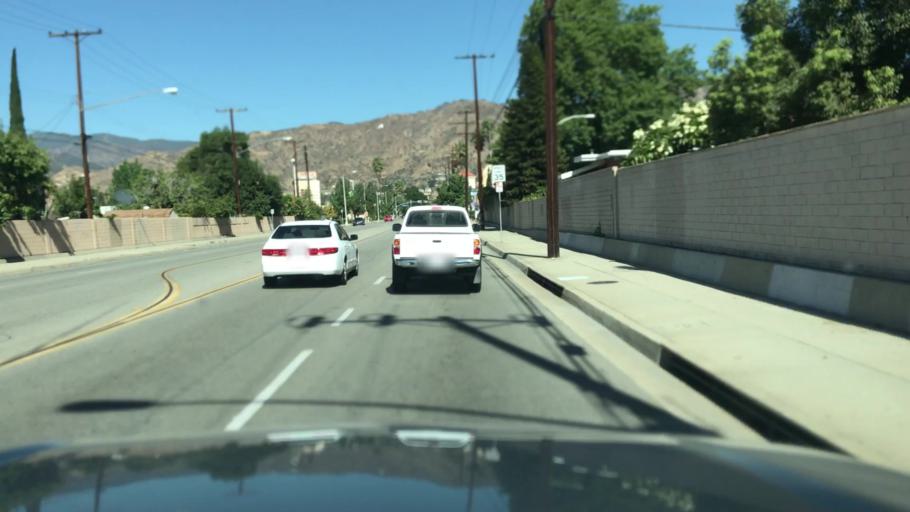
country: US
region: California
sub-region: Los Angeles County
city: Citrus
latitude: 34.1253
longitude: -117.8900
